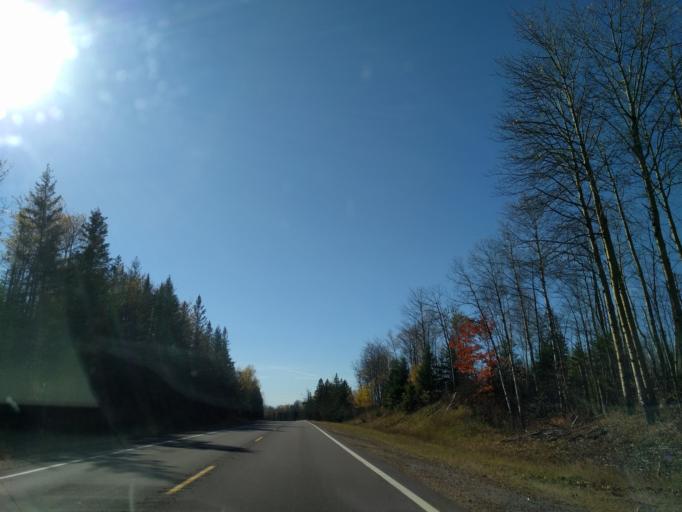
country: US
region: Michigan
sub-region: Marquette County
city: West Ishpeming
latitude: 46.4199
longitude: -87.9856
